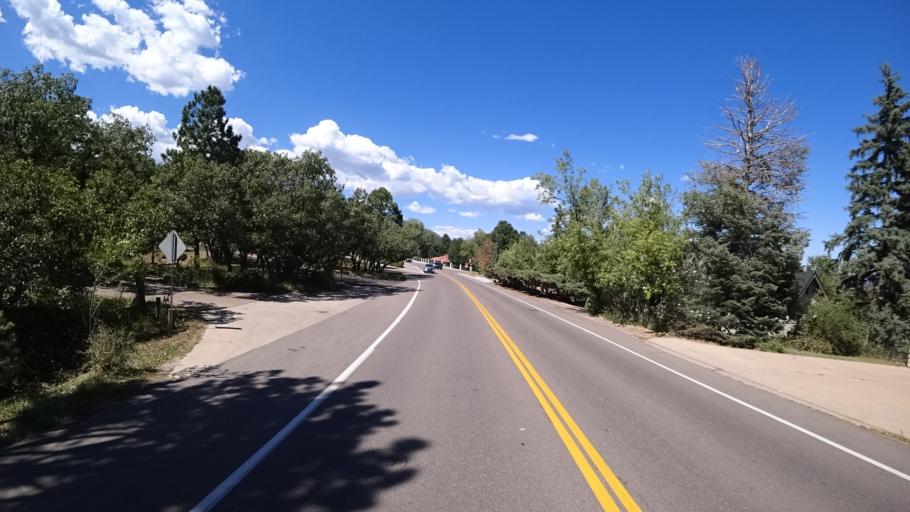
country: US
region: Colorado
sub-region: El Paso County
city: Colorado Springs
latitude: 38.7841
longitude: -104.8551
